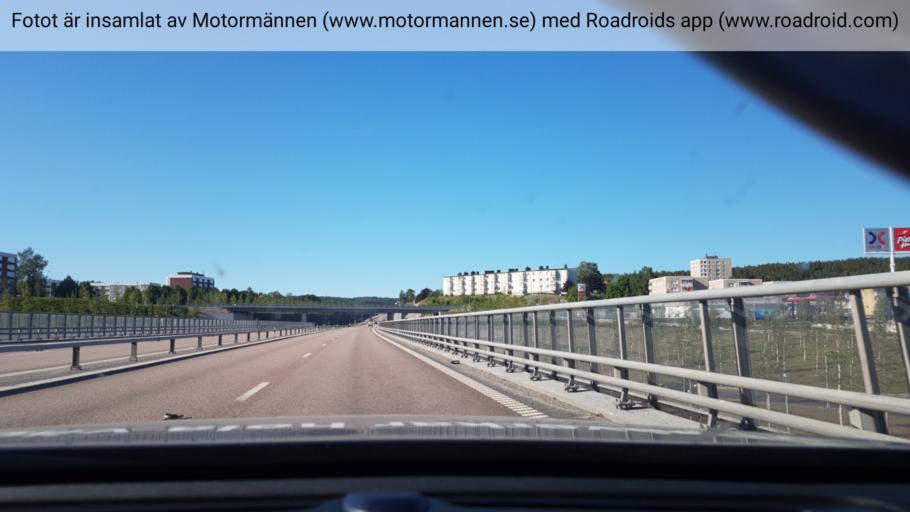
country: SE
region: Vaesternorrland
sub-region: Sundsvalls Kommun
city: Sundsvall
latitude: 62.3962
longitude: 17.3378
